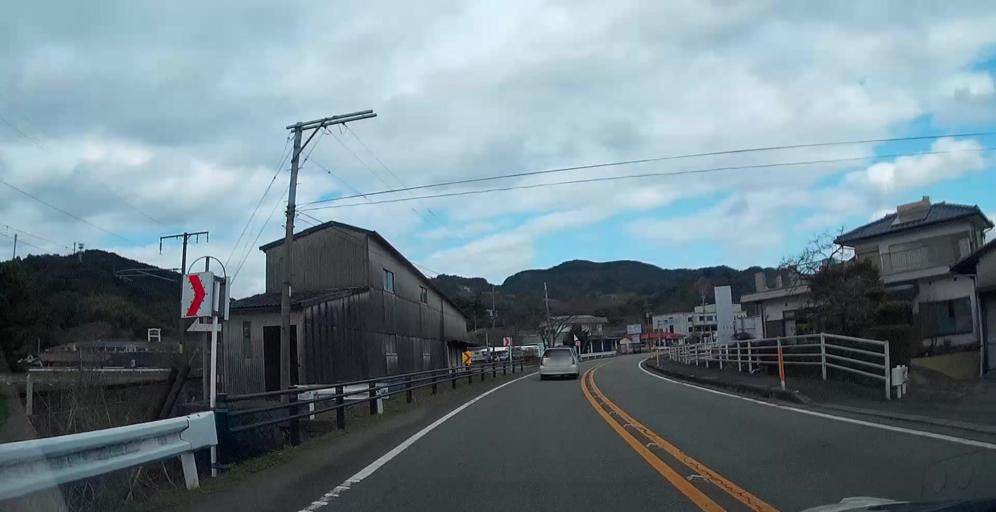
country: JP
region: Kumamoto
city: Yatsushiro
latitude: 32.3622
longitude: 130.5071
